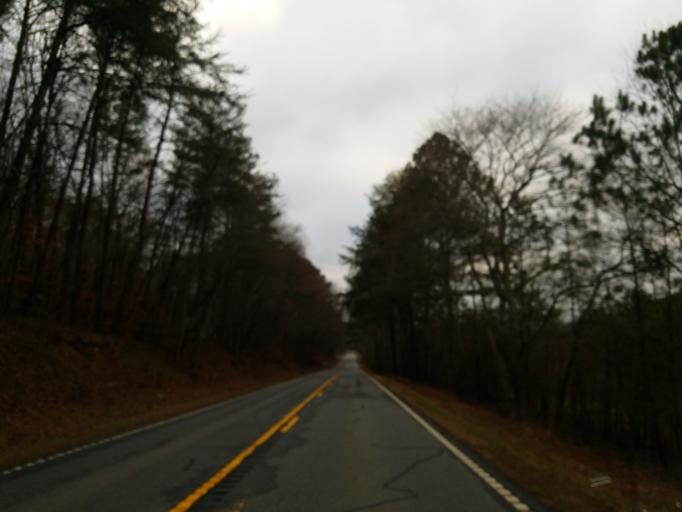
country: US
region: Georgia
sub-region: Bartow County
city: Rydal
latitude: 34.3426
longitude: -84.6134
